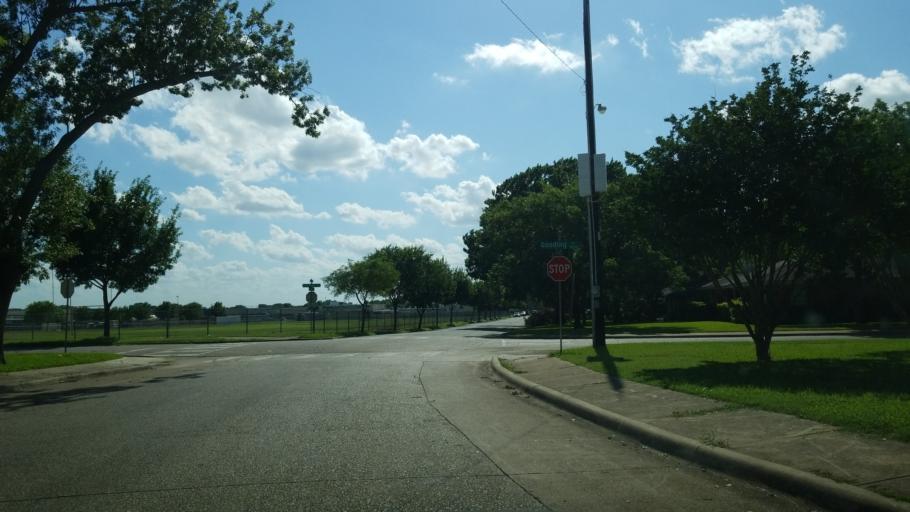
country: US
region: Texas
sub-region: Dallas County
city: University Park
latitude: 32.8835
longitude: -96.8430
